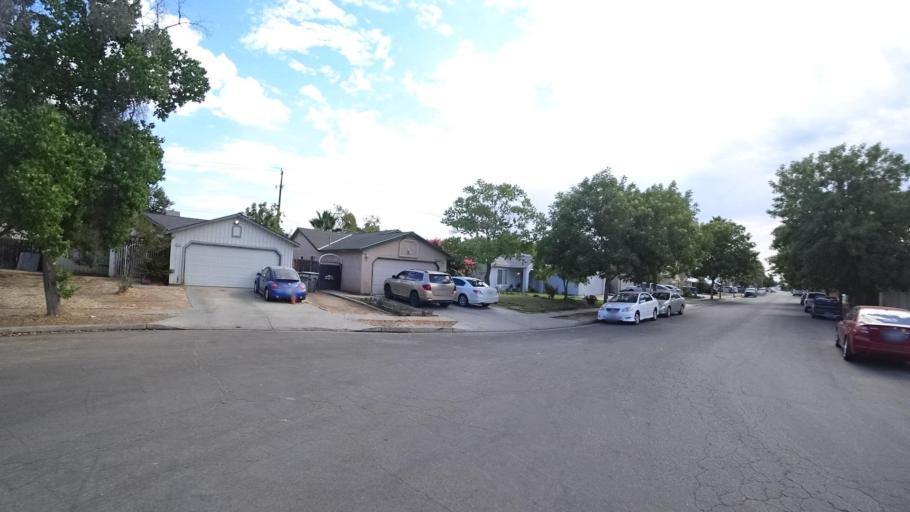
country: US
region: California
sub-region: Fresno County
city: Sunnyside
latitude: 36.7607
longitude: -119.7168
